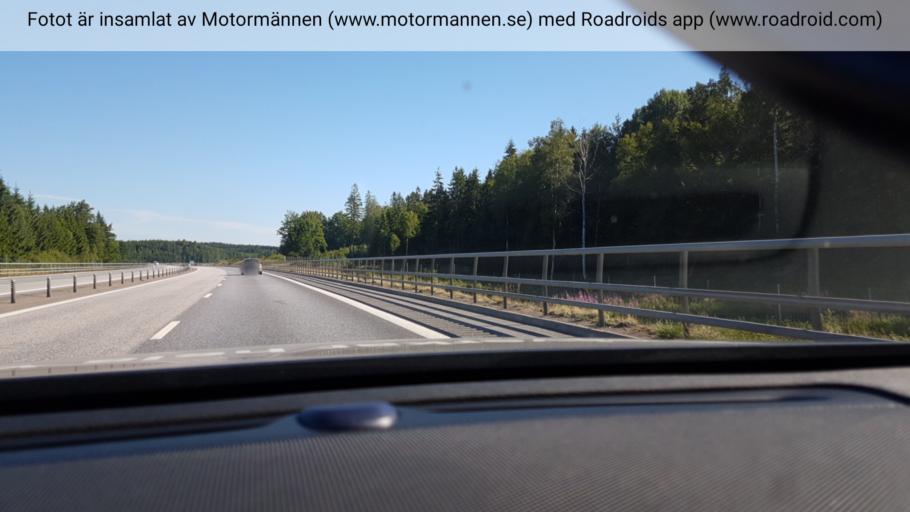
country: SE
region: Kronoberg
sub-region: Markaryds Kommun
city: Markaryd
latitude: 56.4948
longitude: 13.6525
